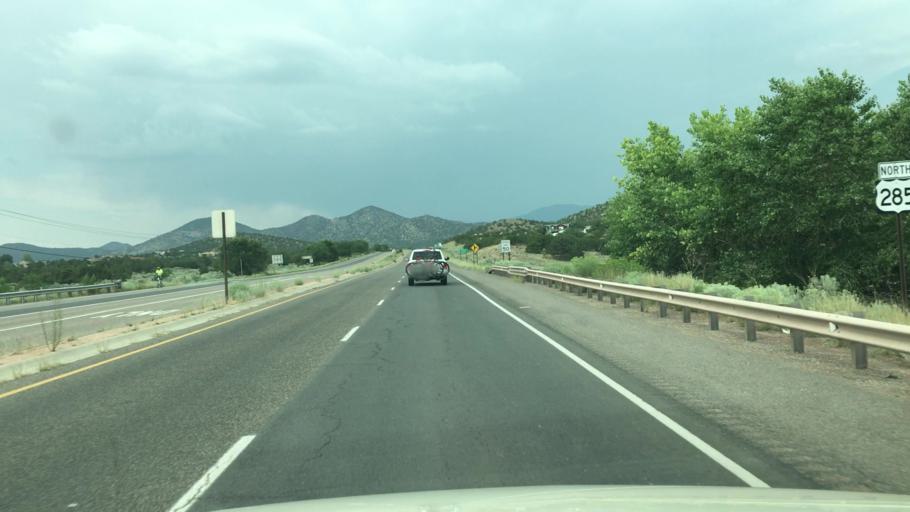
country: US
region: New Mexico
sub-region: Santa Fe County
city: Eldorado at Santa Fe
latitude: 35.5375
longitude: -105.8866
